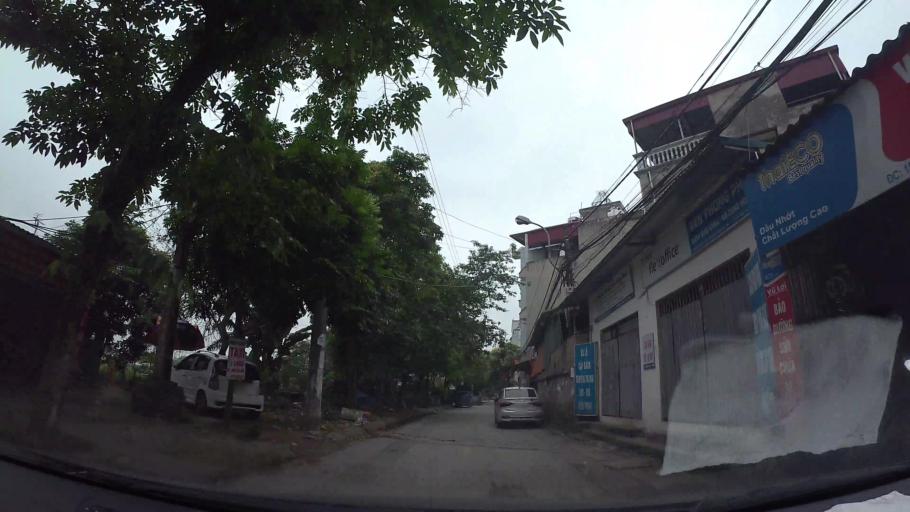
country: VN
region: Hung Yen
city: Van Giang
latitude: 20.9724
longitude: 105.8940
